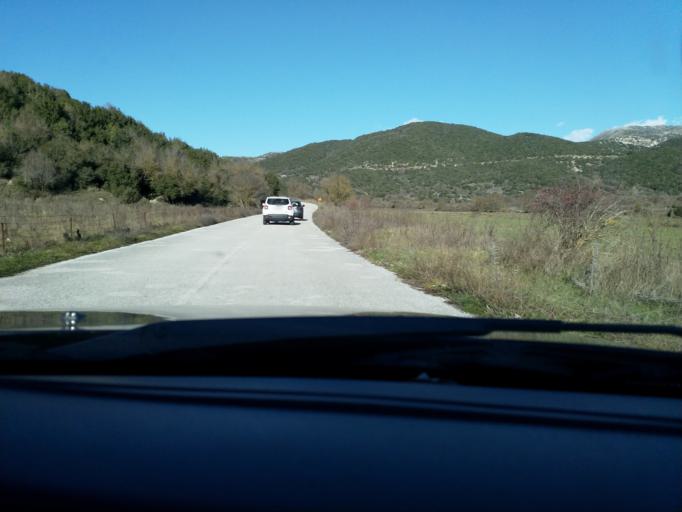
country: GR
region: Epirus
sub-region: Nomos Ioanninon
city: Kalpaki
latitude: 39.8866
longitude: 20.6729
